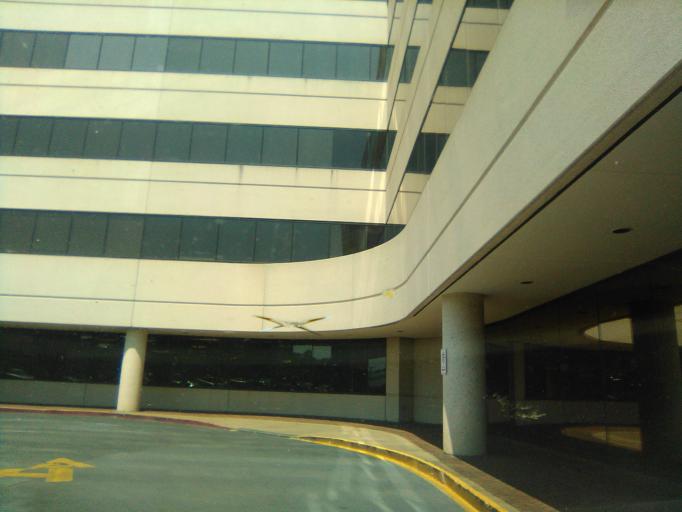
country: US
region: Tennessee
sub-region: Davidson County
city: Belle Meade
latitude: 36.1287
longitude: -86.8443
